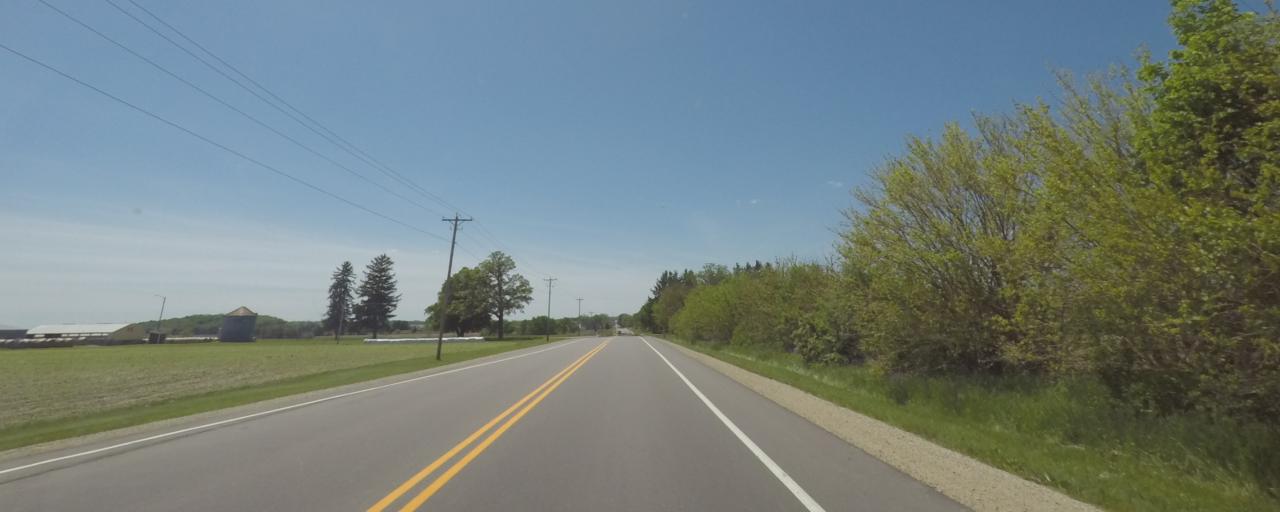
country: US
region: Wisconsin
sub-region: Dane County
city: Oregon
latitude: 42.9503
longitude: -89.4031
